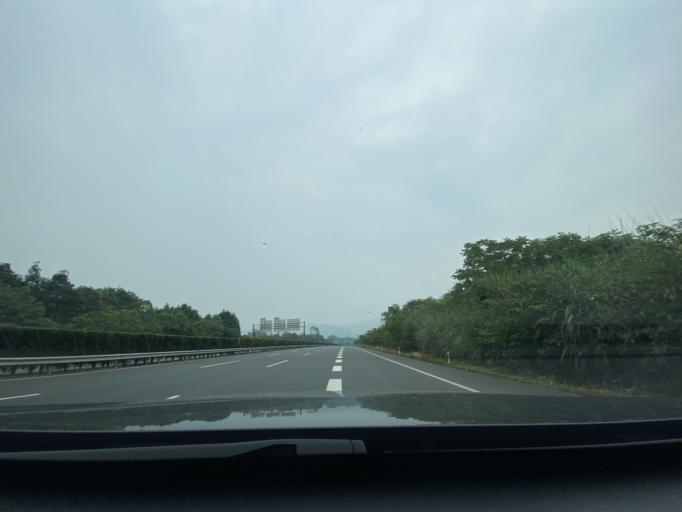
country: CN
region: Sichuan
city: Longquan
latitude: 30.3453
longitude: 104.1279
